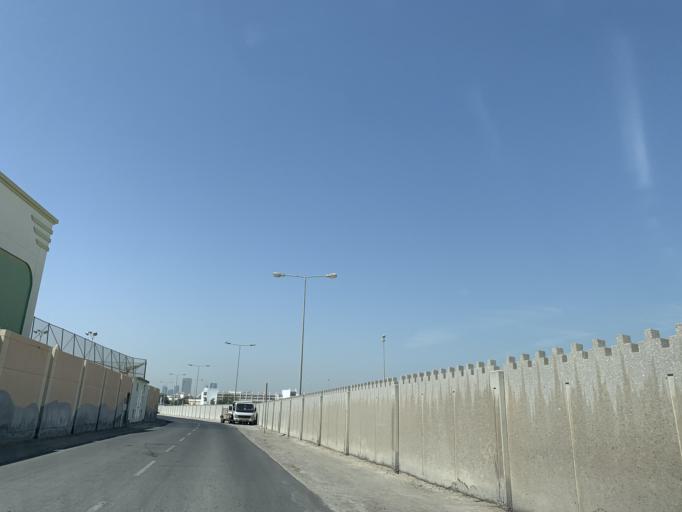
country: BH
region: Muharraq
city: Al Muharraq
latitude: 26.2642
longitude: 50.6131
